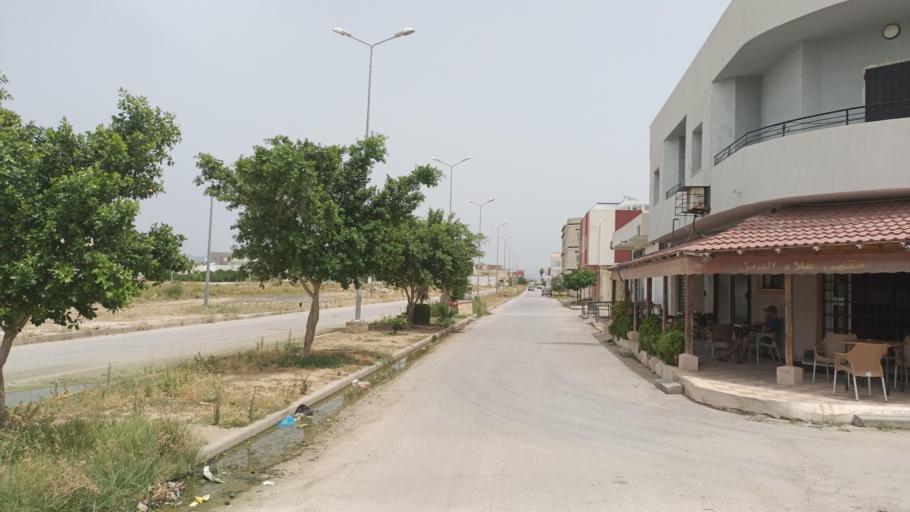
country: TN
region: Nabul
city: Manzil Bu Zalafah
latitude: 36.7010
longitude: 10.4823
